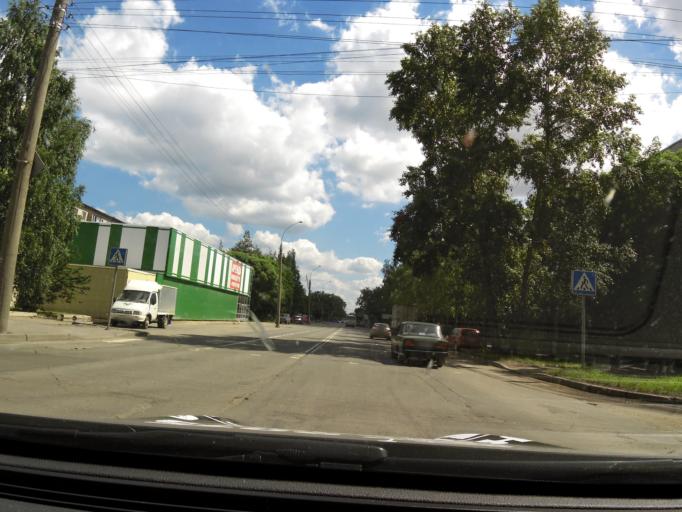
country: RU
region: Vologda
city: Vologda
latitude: 59.2266
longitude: 39.8634
